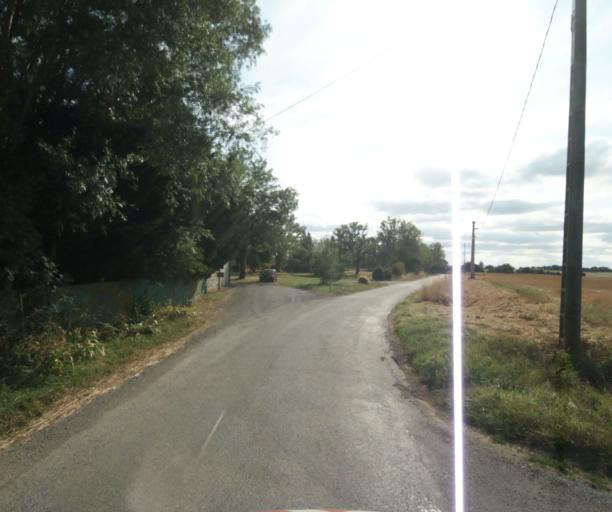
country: FR
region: Midi-Pyrenees
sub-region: Departement du Tarn
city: Puylaurens
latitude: 43.5256
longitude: 2.0022
